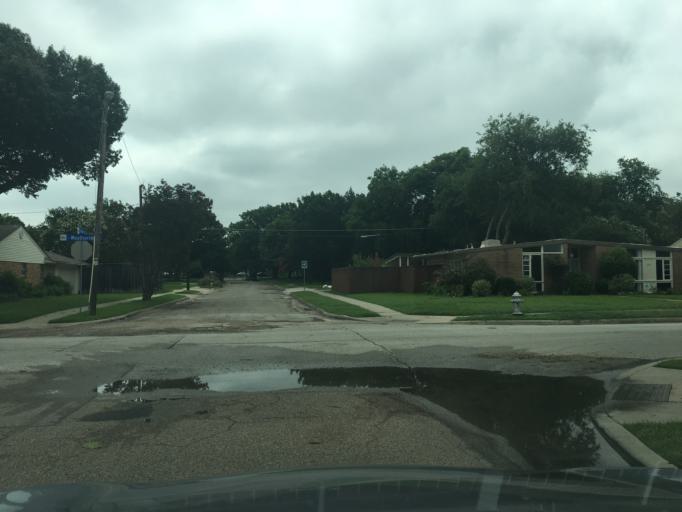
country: US
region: Texas
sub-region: Dallas County
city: Richardson
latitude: 32.9486
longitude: -96.7488
